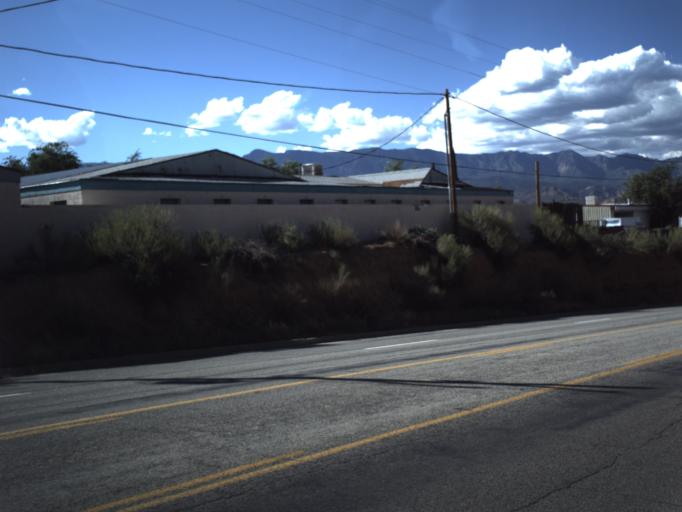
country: US
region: Utah
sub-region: Washington County
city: LaVerkin
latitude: 37.2137
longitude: -113.2721
